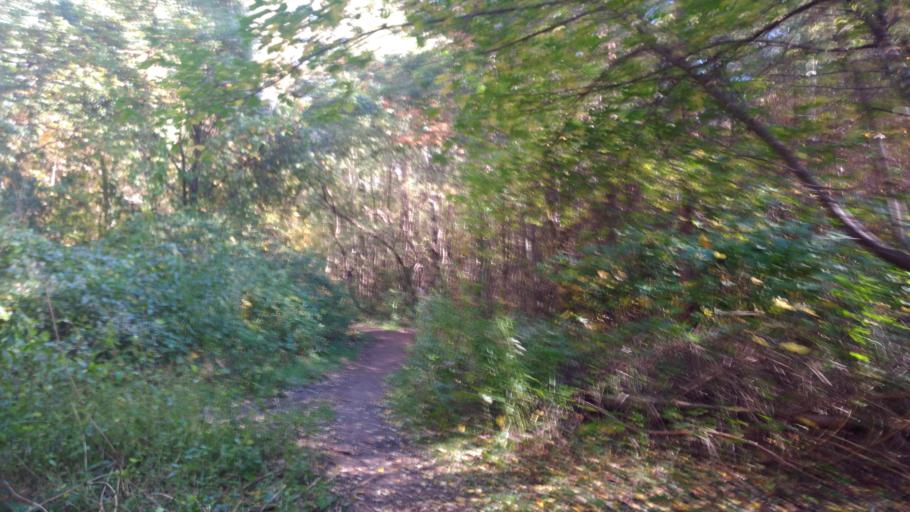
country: DE
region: Saxony
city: Albertstadt
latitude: 51.1070
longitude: 13.7527
